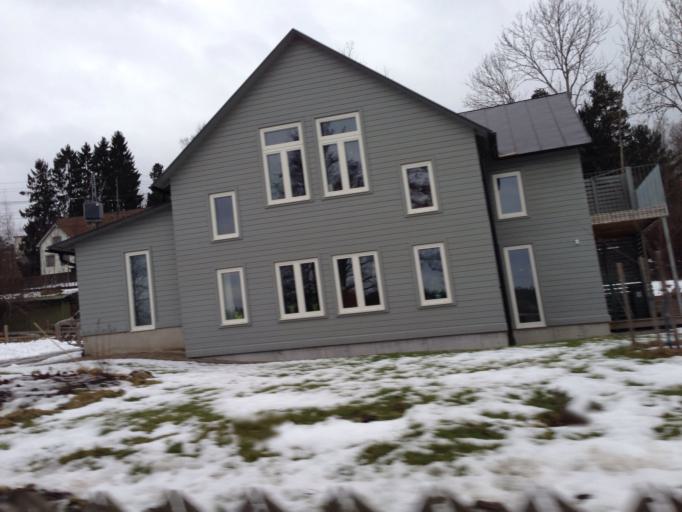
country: SE
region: Stockholm
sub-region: Salems Kommun
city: Ronninge
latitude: 59.1925
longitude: 17.7378
